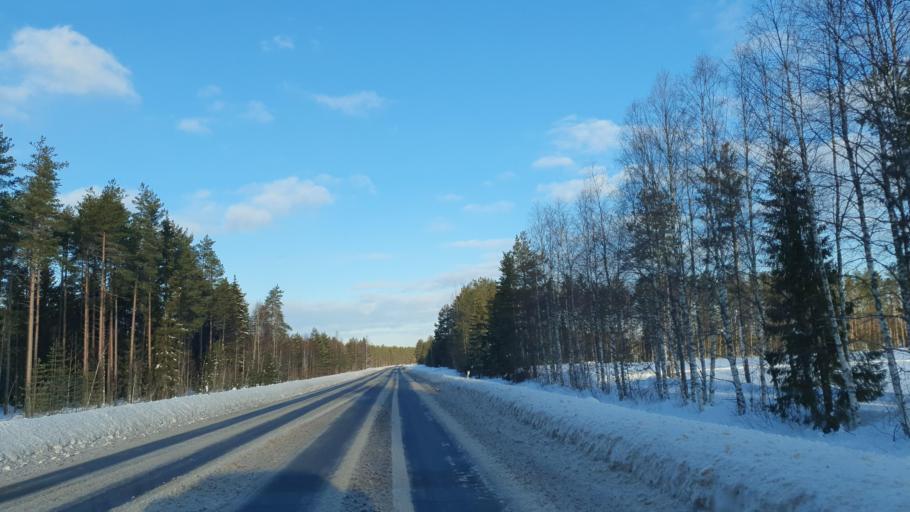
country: FI
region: Northern Ostrobothnia
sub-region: Oulunkaari
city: Utajaervi
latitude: 64.7017
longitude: 26.5269
